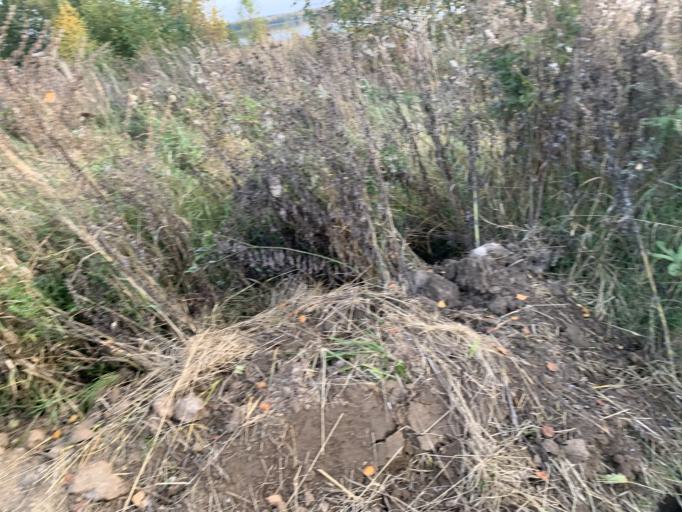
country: RU
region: Jaroslavl
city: Petrovsk
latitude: 56.9793
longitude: 39.3788
